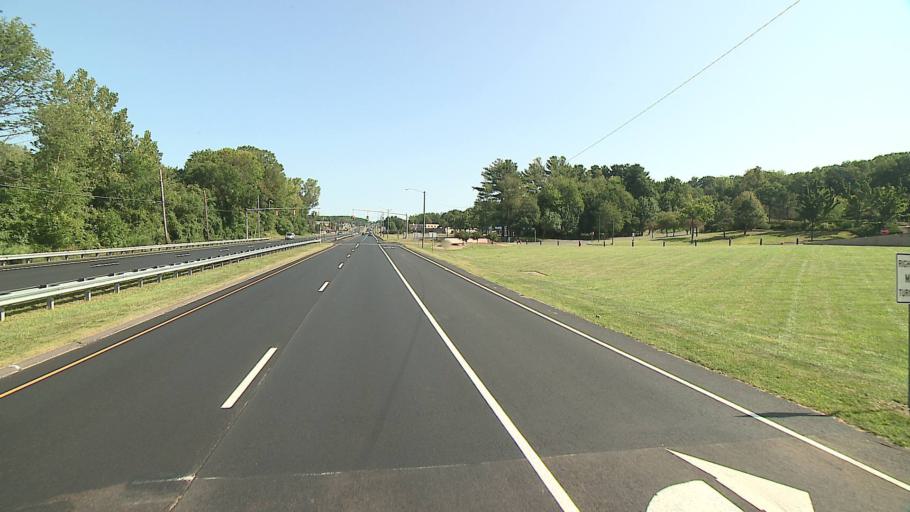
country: US
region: Connecticut
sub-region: Hartford County
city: Newington
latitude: 41.6741
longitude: -72.7153
